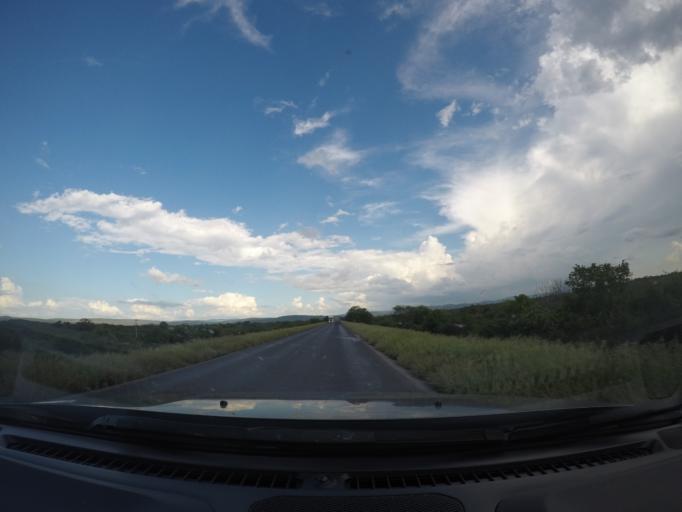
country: BR
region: Bahia
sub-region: Ibotirama
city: Ibotirama
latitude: -12.1716
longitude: -43.2621
